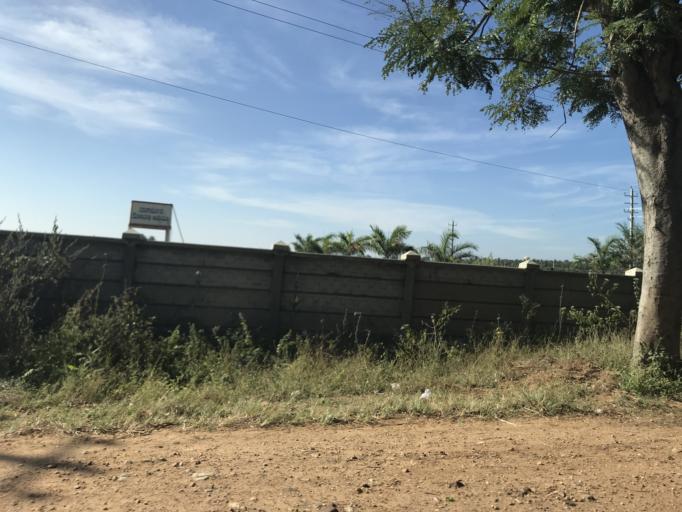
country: IN
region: Karnataka
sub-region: Mysore
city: Mysore
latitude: 12.2284
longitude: 76.5882
